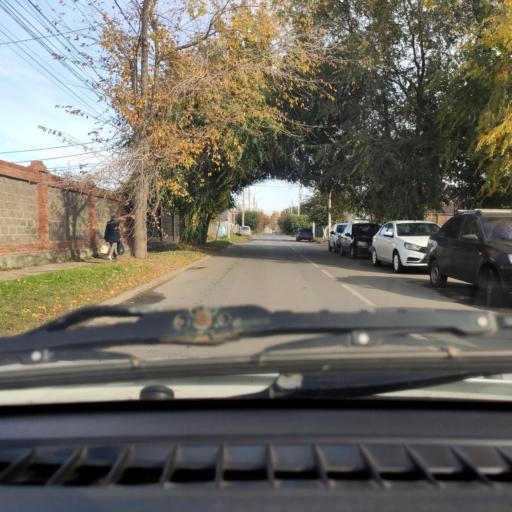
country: RU
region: Samara
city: Tol'yatti
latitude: 53.5223
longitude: 49.4029
